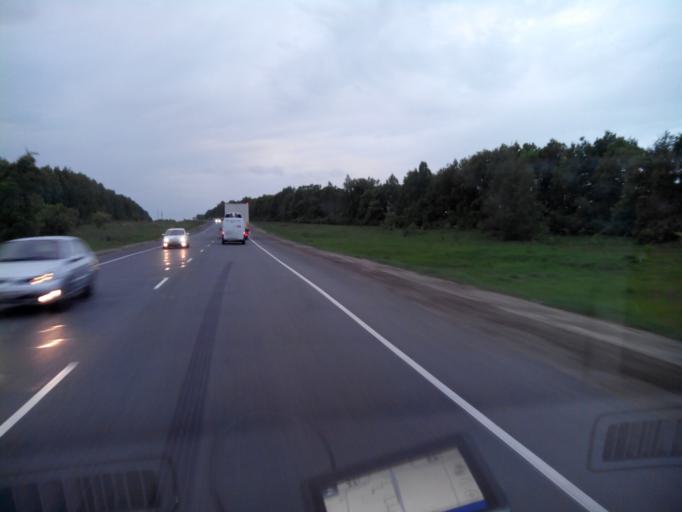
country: RU
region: Penza
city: Chemodanovka
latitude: 53.2243
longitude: 45.3322
